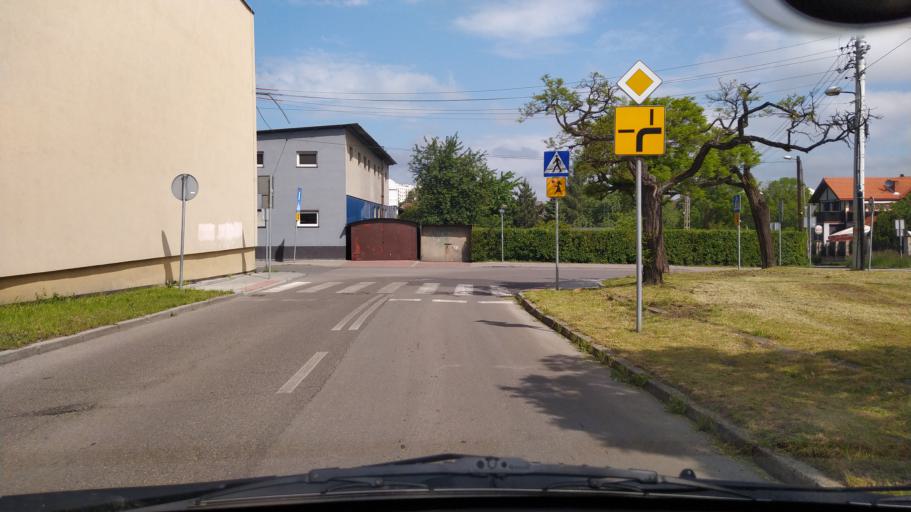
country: PL
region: Silesian Voivodeship
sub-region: Powiat gliwicki
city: Przyszowice
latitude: 50.2894
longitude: 18.7329
